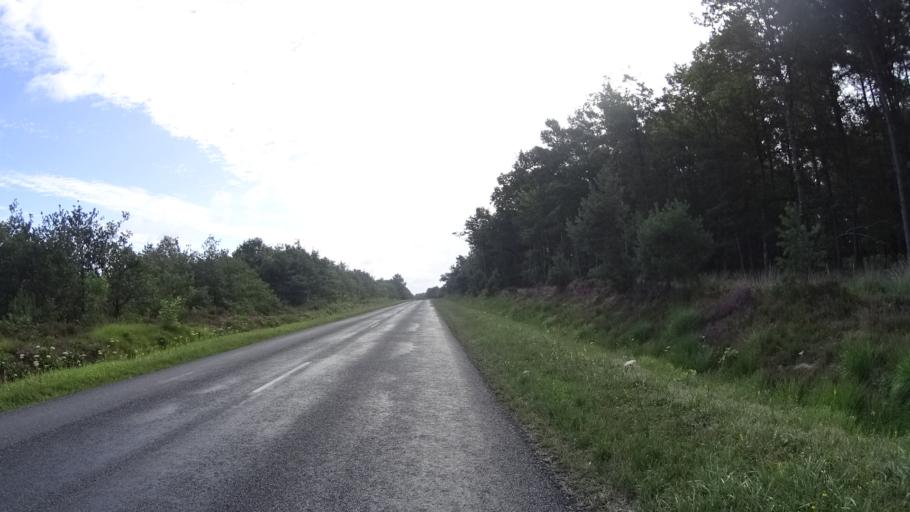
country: FR
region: Centre
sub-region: Departement du Loiret
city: Bouzy-la-Foret
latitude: 47.8688
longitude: 2.4147
